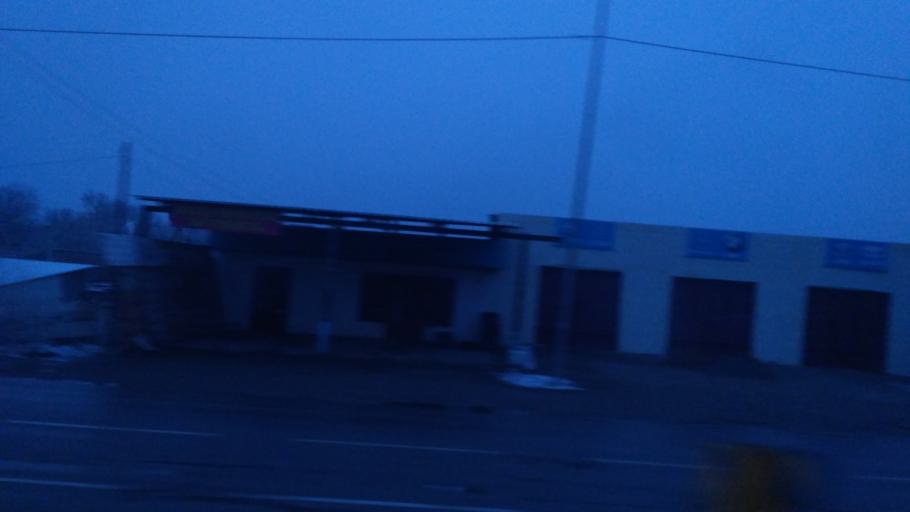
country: KZ
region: Ongtustik Qazaqstan
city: Shymkent
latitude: 42.3492
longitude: 69.5353
